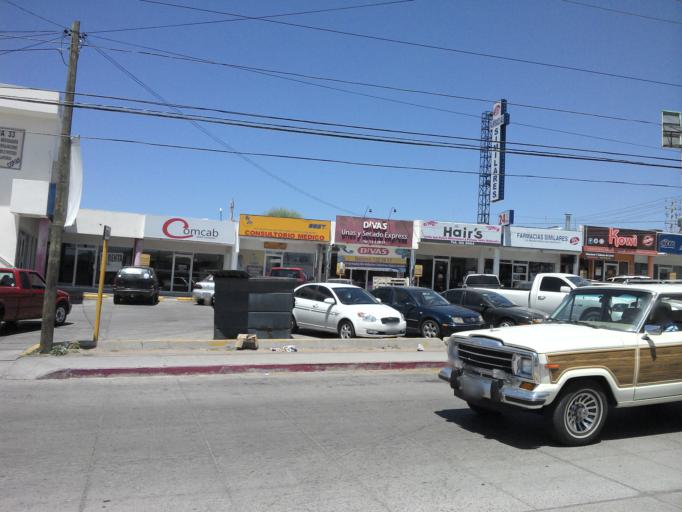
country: MX
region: Sonora
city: Heroica Guaymas
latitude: 27.9252
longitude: -110.9181
